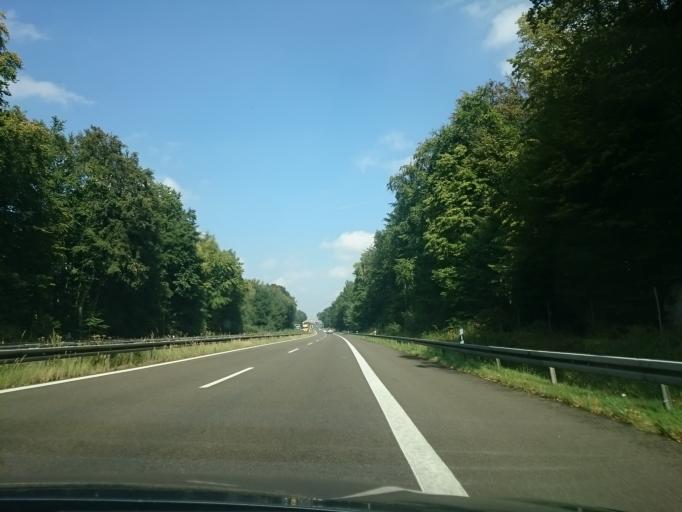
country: DE
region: Brandenburg
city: Gramzow
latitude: 53.1687
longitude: 13.9188
